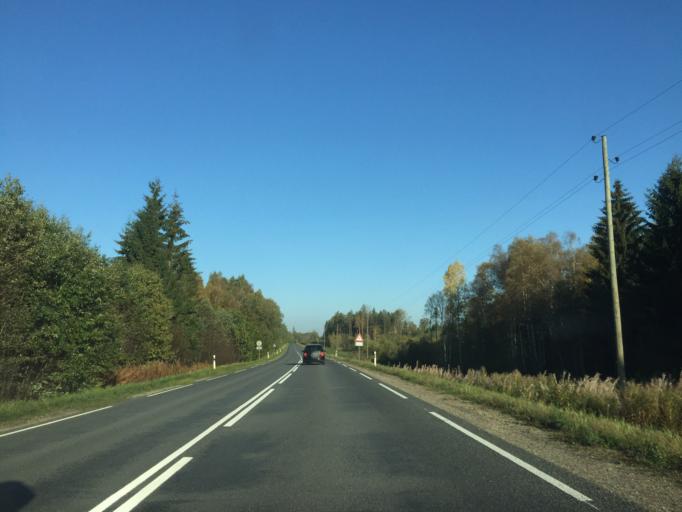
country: LV
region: Raunas
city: Rauna
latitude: 57.2275
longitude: 25.5785
